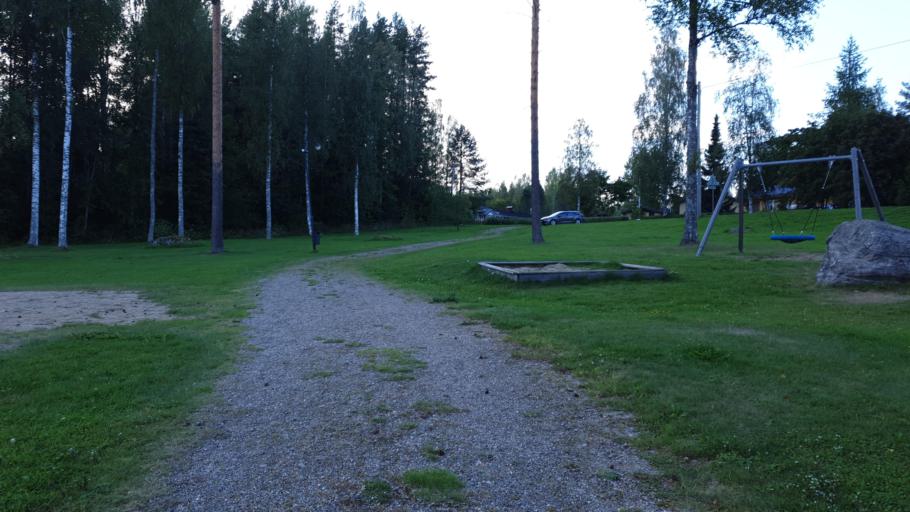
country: FI
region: Northern Savo
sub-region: Koillis-Savo
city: Kaavi
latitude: 62.9742
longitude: 28.4684
